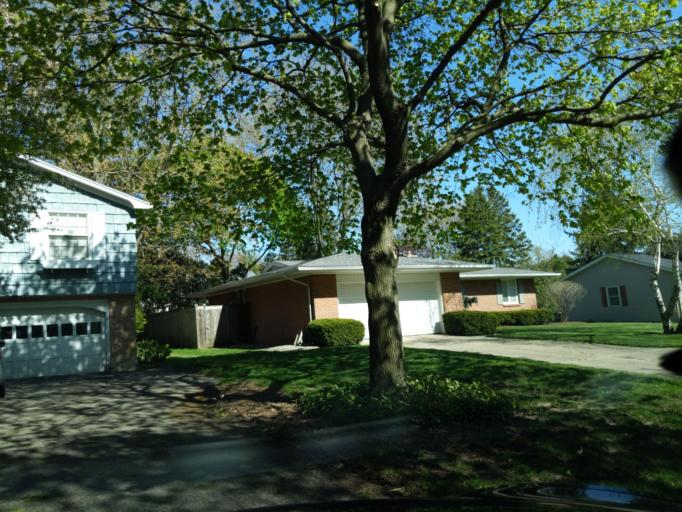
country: US
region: Michigan
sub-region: Kent County
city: East Grand Rapids
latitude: 42.9694
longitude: -85.6153
